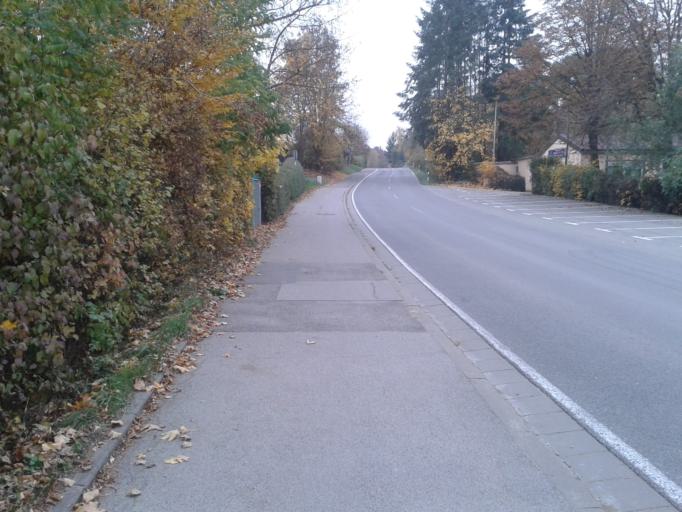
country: DE
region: Bavaria
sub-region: Upper Franconia
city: Gundelsheim
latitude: 49.9291
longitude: 10.9236
